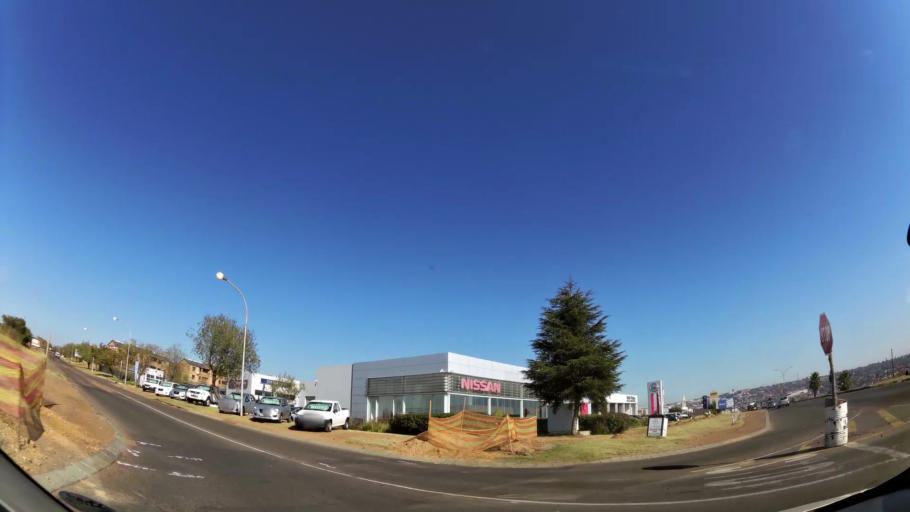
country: ZA
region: Mpumalanga
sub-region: Nkangala District Municipality
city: Witbank
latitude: -25.8821
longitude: 29.2568
